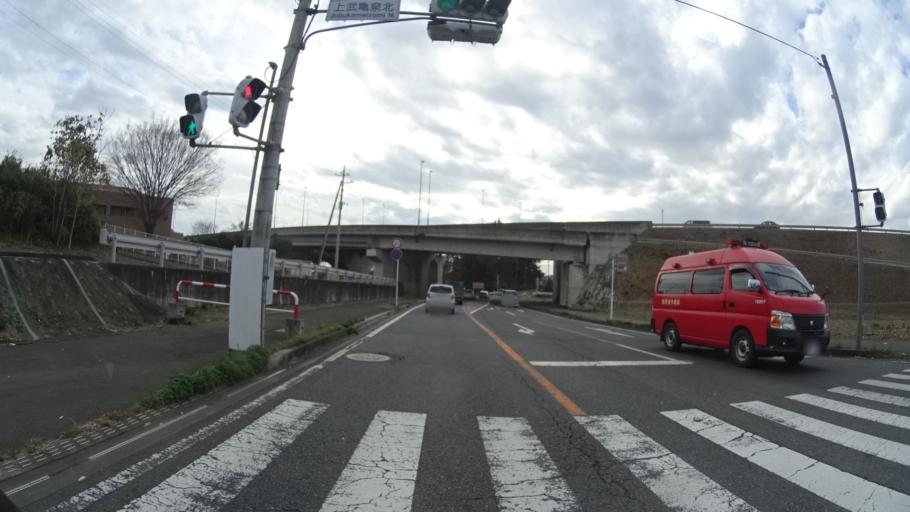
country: JP
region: Gunma
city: Maebashi-shi
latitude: 36.4055
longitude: 139.1263
